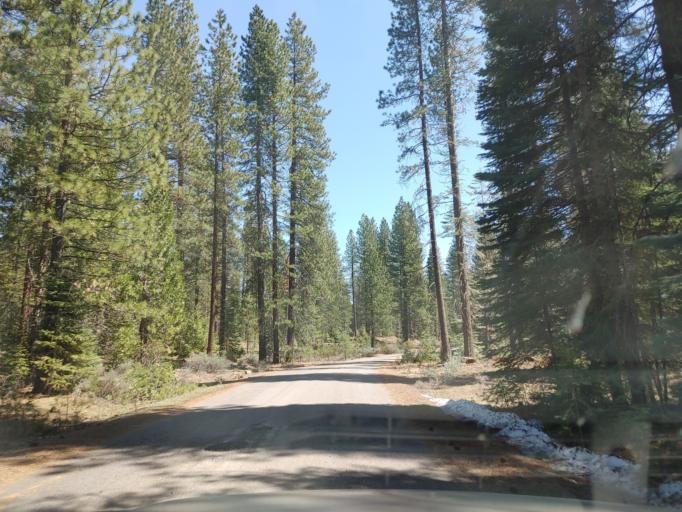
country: US
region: California
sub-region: Siskiyou County
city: McCloud
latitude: 41.2536
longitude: -121.9466
